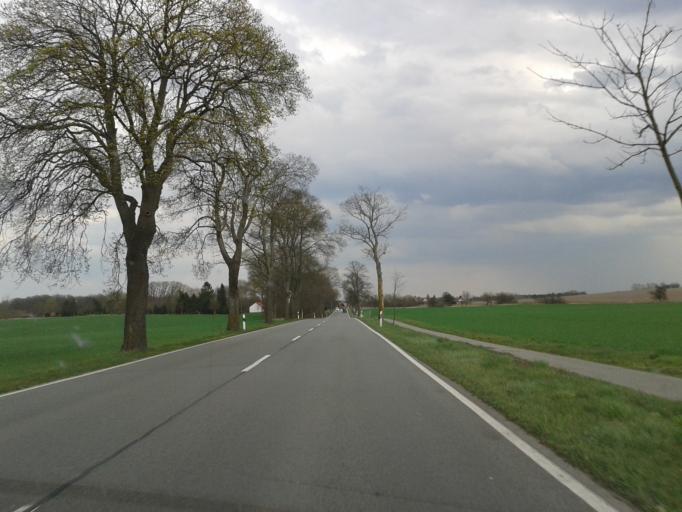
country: DE
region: Saxony-Anhalt
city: Wallstawe
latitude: 52.8776
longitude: 11.0544
